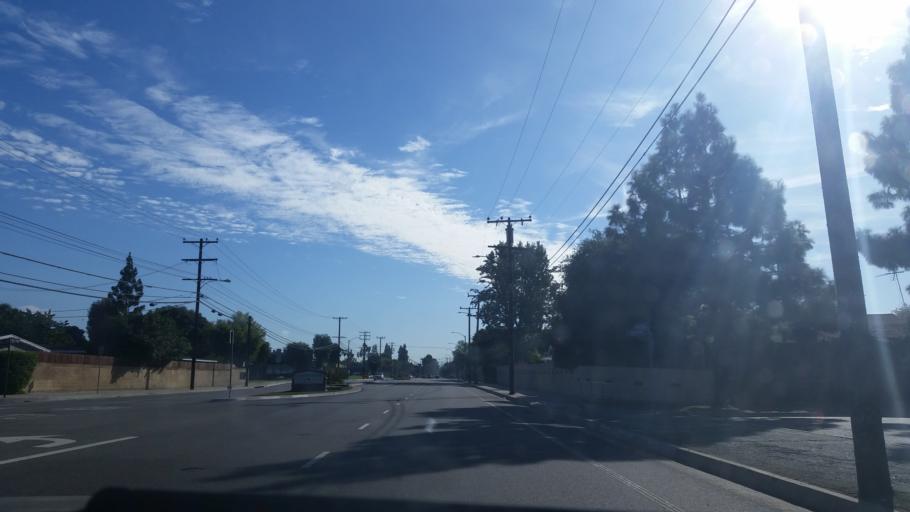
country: US
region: California
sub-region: Los Angeles County
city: Hawaiian Gardens
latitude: 33.8459
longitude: -118.0864
